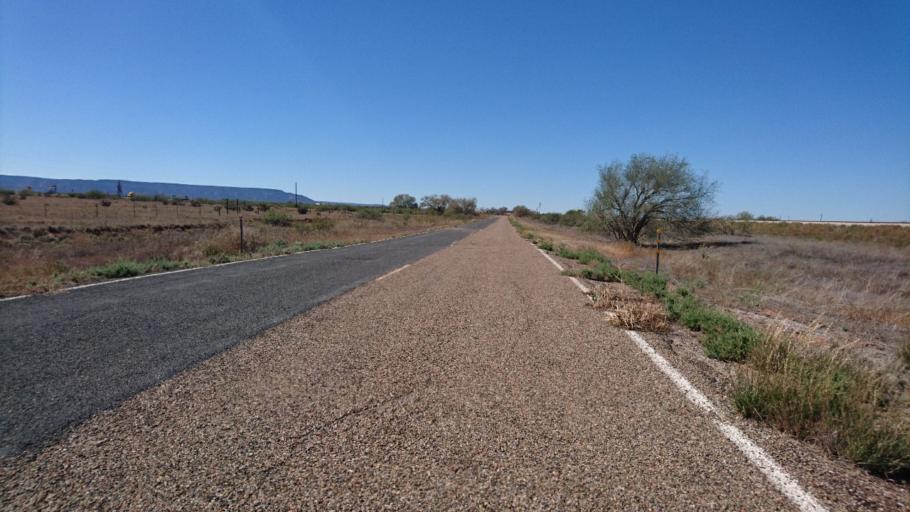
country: US
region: New Mexico
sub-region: Quay County
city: Tucumcari
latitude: 35.0982
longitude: -104.0573
